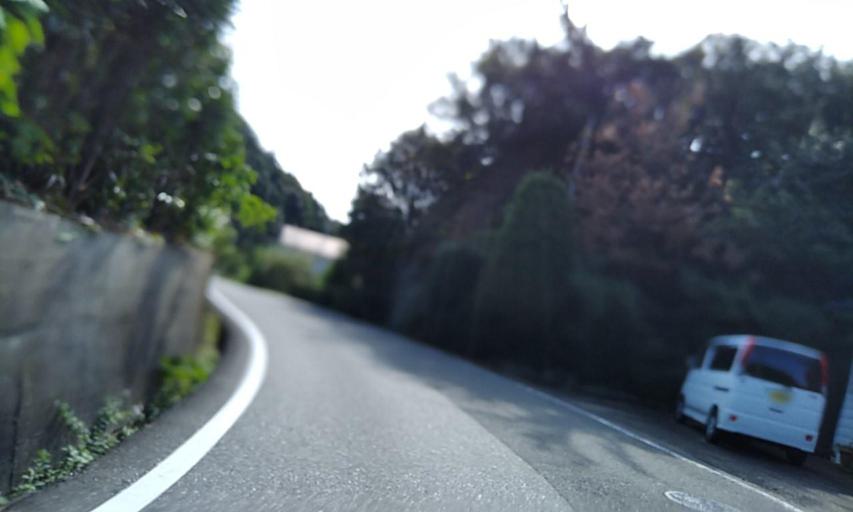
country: JP
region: Wakayama
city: Gobo
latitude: 33.9668
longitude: 135.1027
